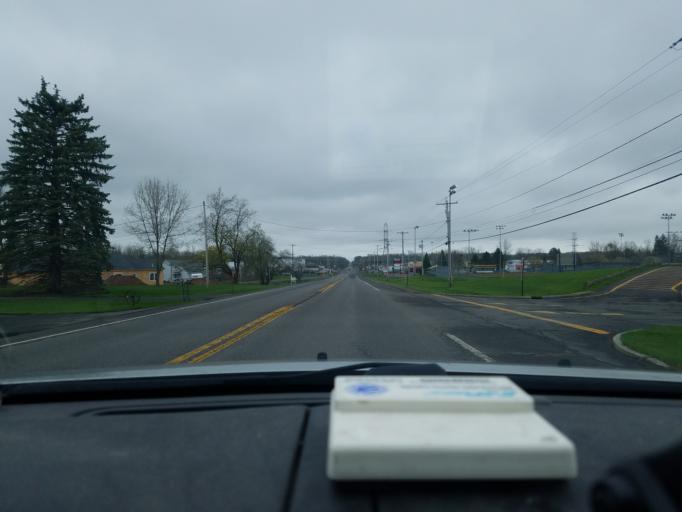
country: US
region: New York
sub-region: Onondaga County
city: North Syracuse
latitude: 43.1609
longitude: -76.0978
